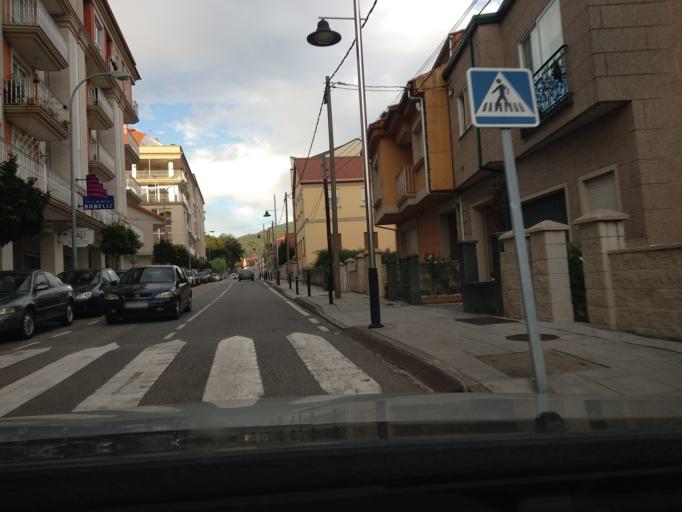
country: ES
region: Galicia
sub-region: Provincia de Pontevedra
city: Moana
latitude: 42.2882
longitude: -8.7333
